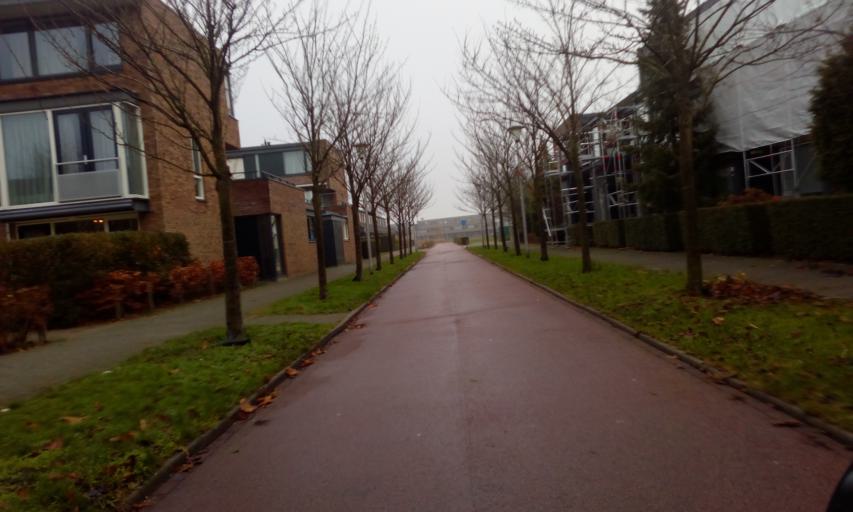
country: NL
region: South Holland
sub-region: Gemeente Lansingerland
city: Berkel en Rodenrijs
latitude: 51.9956
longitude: 4.4634
